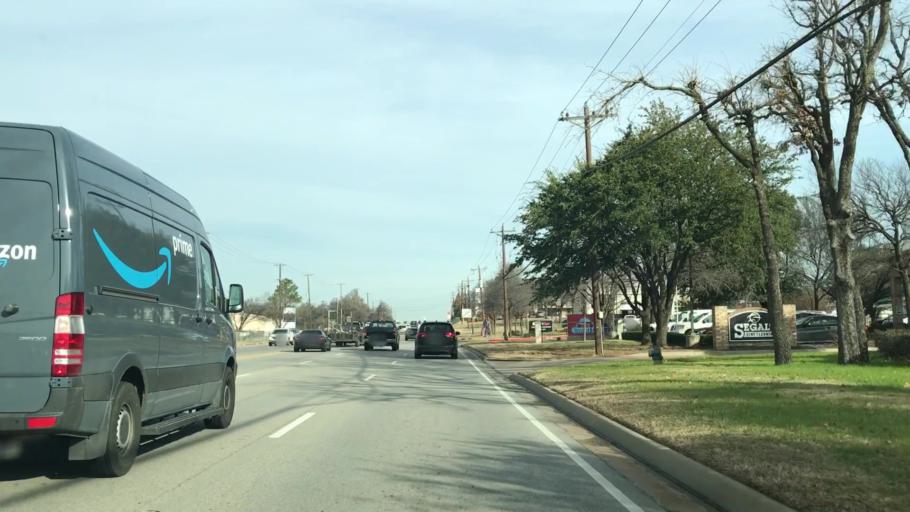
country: US
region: Texas
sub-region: Tarrant County
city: Southlake
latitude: 32.9275
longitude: -97.1858
